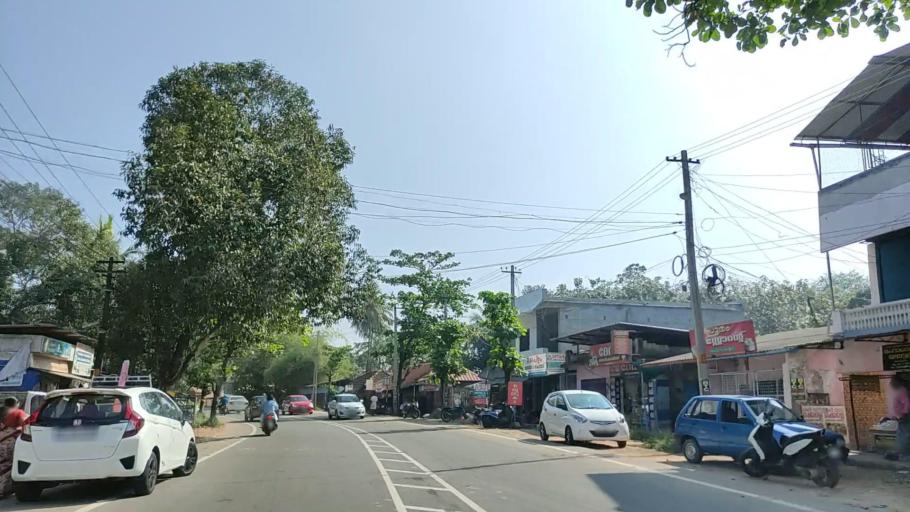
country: IN
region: Kerala
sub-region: Kollam
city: Punalur
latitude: 8.9299
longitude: 76.9320
